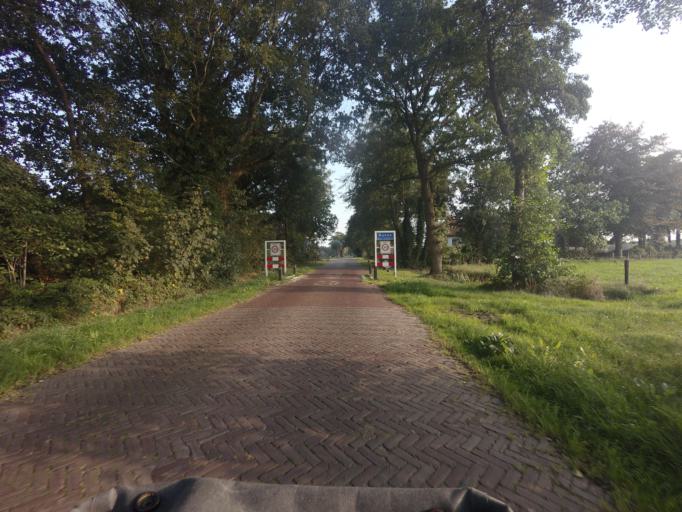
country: NL
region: Drenthe
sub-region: Gemeente Tynaarlo
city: Vries
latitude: 53.1215
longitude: 6.5325
